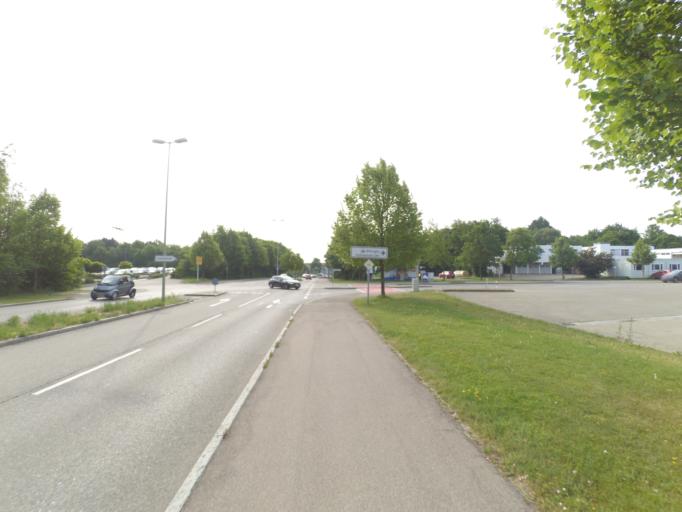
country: DE
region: Baden-Wuerttemberg
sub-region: Tuebingen Region
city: Ulm
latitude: 48.4263
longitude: 10.0096
